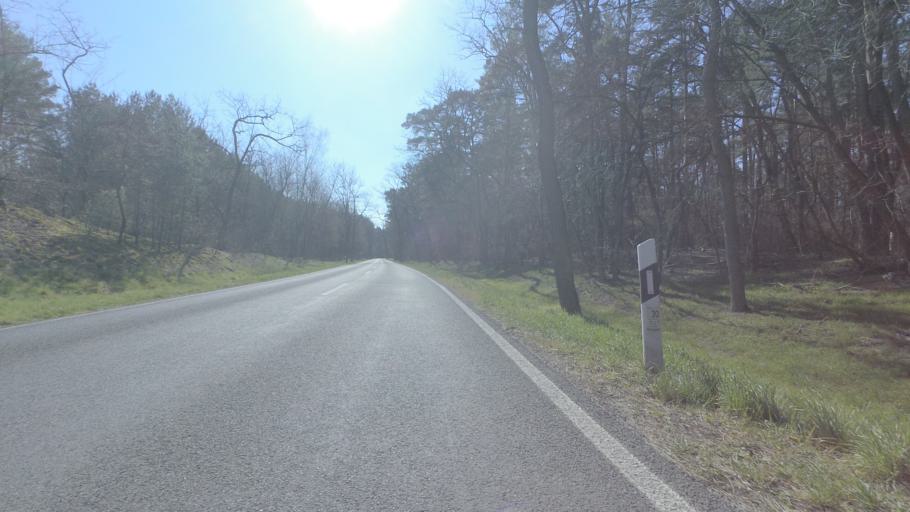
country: DE
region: Brandenburg
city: Munchehofe
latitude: 52.1162
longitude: 13.7795
